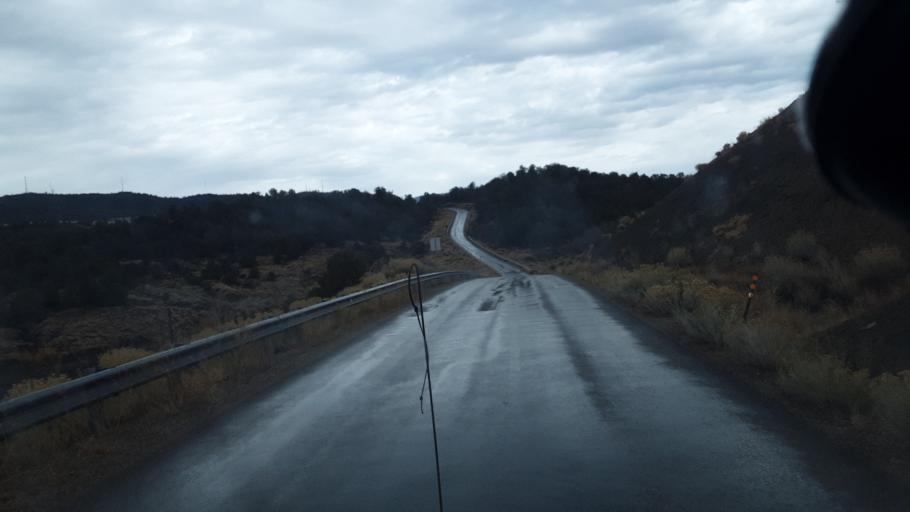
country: US
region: Colorado
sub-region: La Plata County
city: Durango
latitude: 37.2365
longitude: -107.9075
